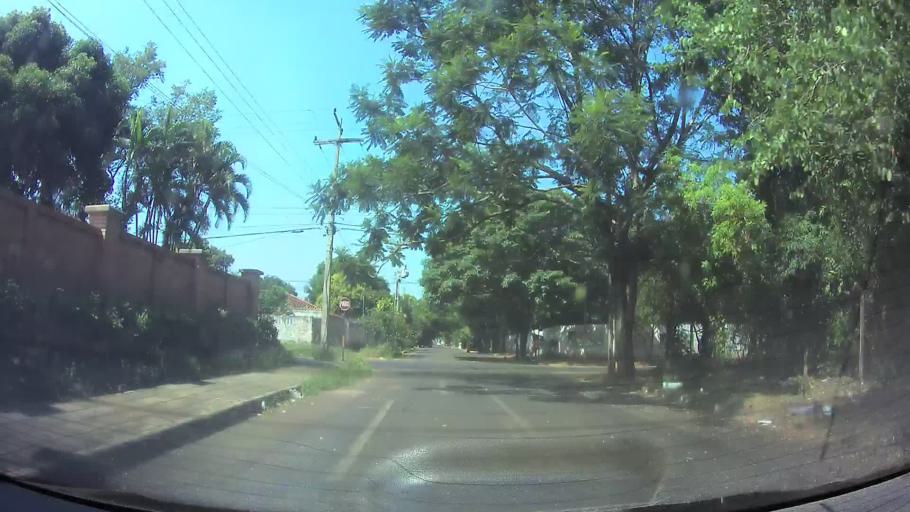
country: PY
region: Central
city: San Lorenzo
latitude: -25.2683
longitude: -57.4992
